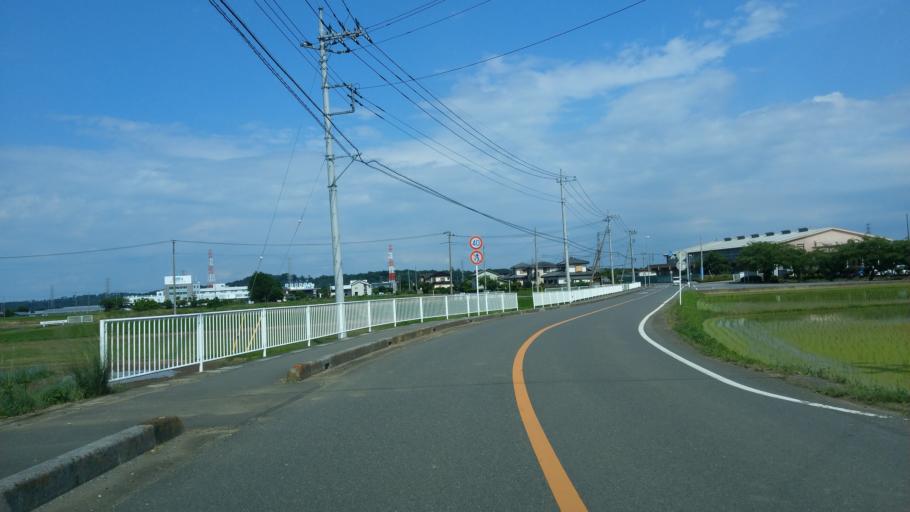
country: JP
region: Saitama
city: Kodamacho-kodamaminami
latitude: 36.1815
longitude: 139.1750
